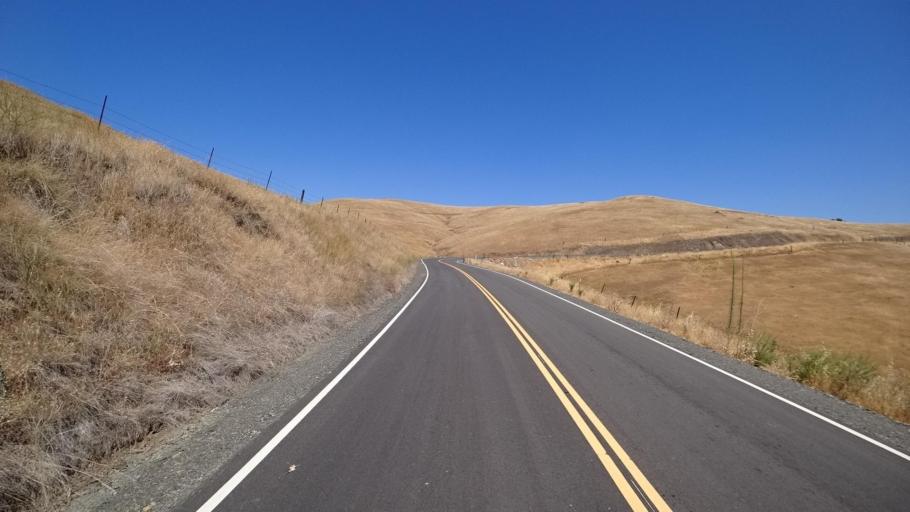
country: US
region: California
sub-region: Mariposa County
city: Mariposa
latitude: 37.3446
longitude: -119.9652
